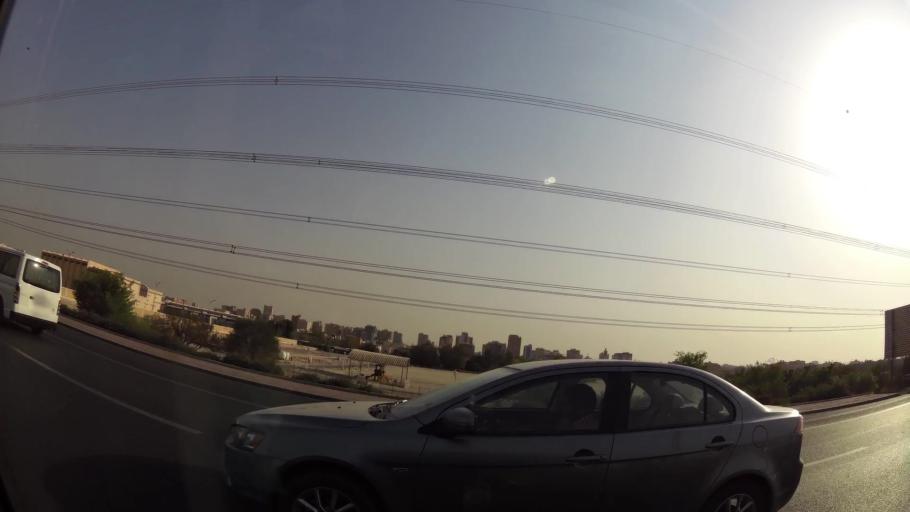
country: KW
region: Al Farwaniyah
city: Al Farwaniyah
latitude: 29.3031
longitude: 47.9691
